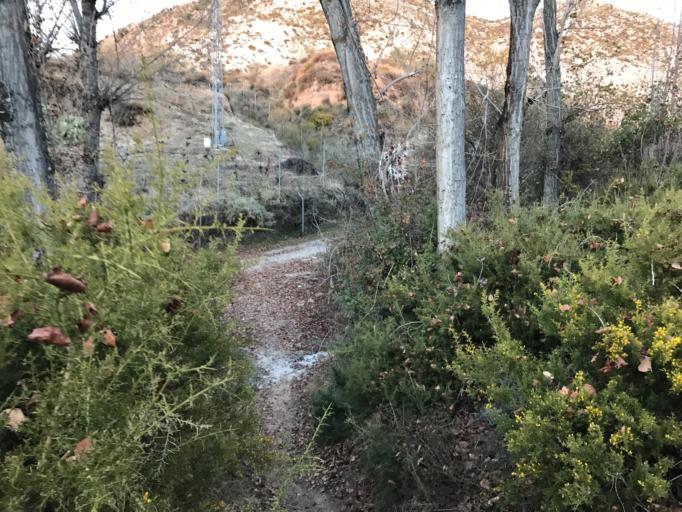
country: ES
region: Andalusia
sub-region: Provincia de Granada
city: Beas de Granada
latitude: 37.2284
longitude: -3.4735
